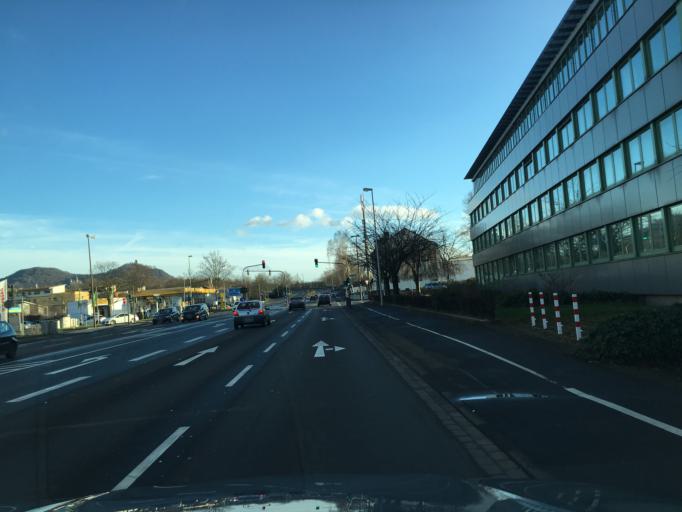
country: DE
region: North Rhine-Westphalia
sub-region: Regierungsbezirk Koln
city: Konigswinter
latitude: 50.6770
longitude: 7.1689
